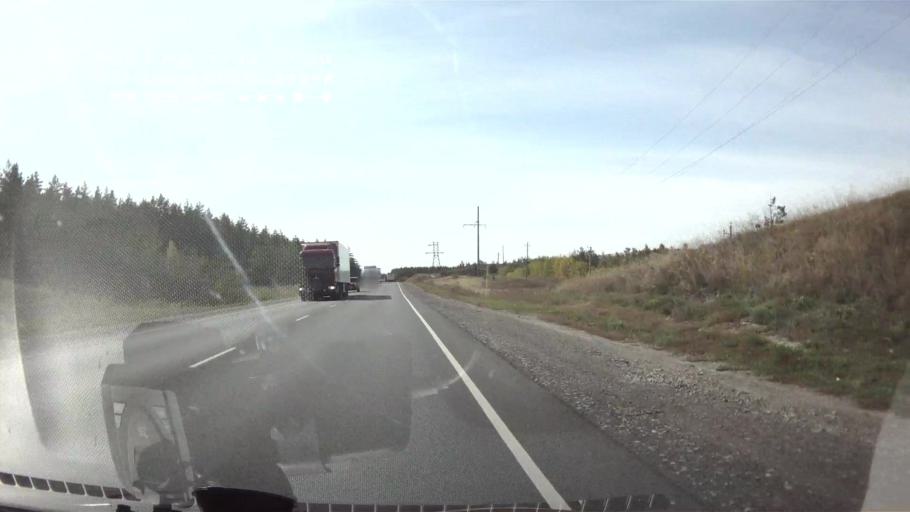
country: RU
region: Saratov
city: Khvalynsk
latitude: 52.5375
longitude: 48.0463
